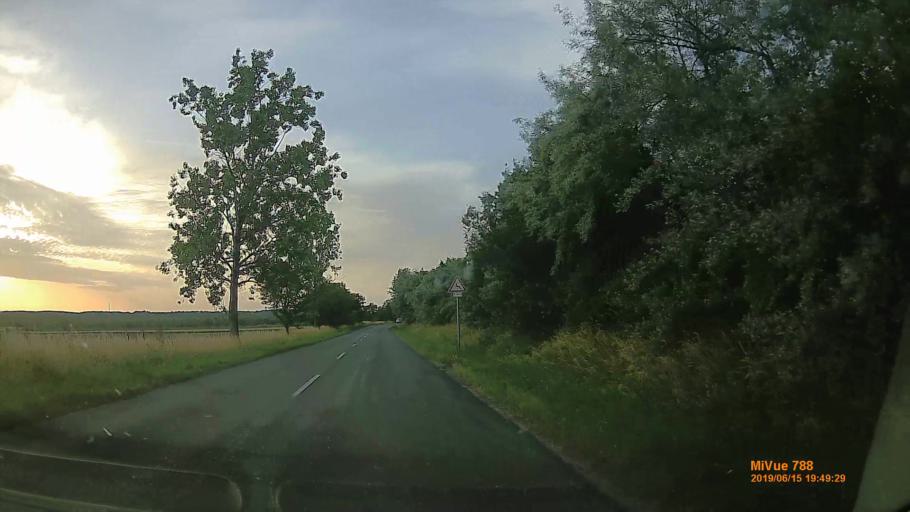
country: HU
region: Veszprem
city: Szentkiralyszabadja
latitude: 47.0352
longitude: 17.9325
